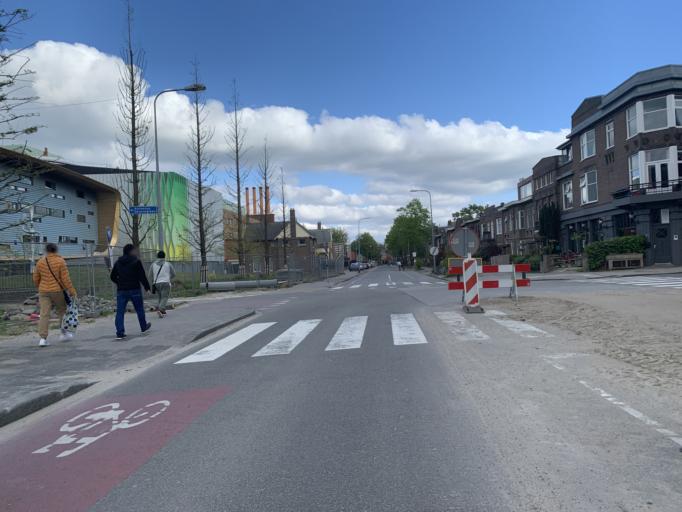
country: NL
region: Groningen
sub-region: Gemeente Groningen
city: Groningen
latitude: 53.2237
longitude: 6.5698
